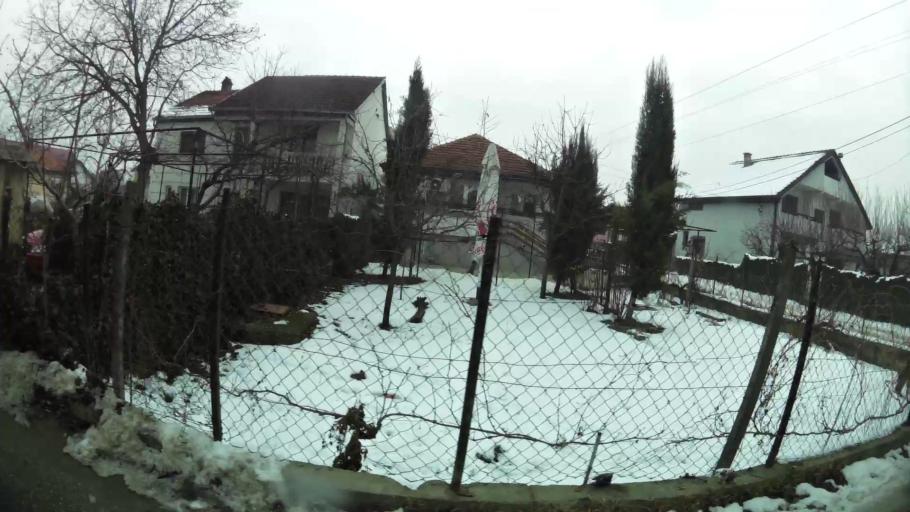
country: MK
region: Saraj
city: Saraj
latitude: 42.0323
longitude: 21.3534
